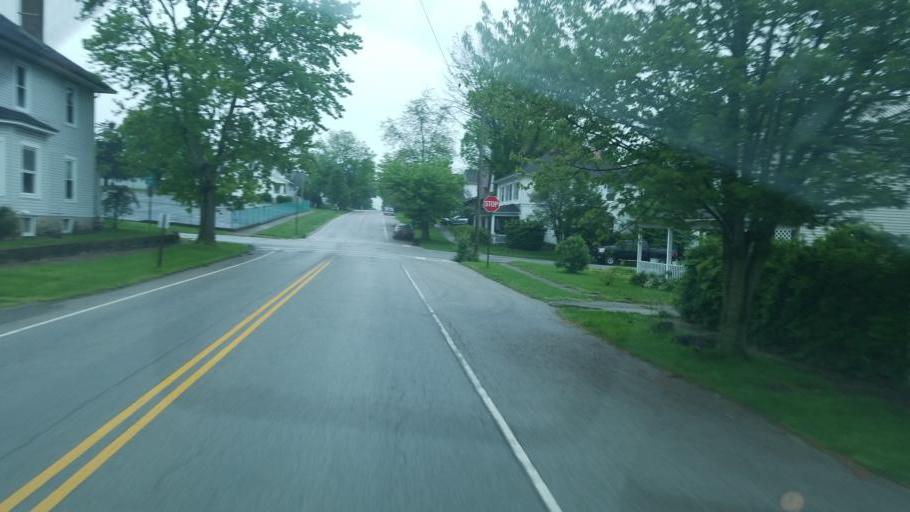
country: US
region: Ohio
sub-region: Highland County
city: Hillsboro
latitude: 39.2000
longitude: -83.6152
